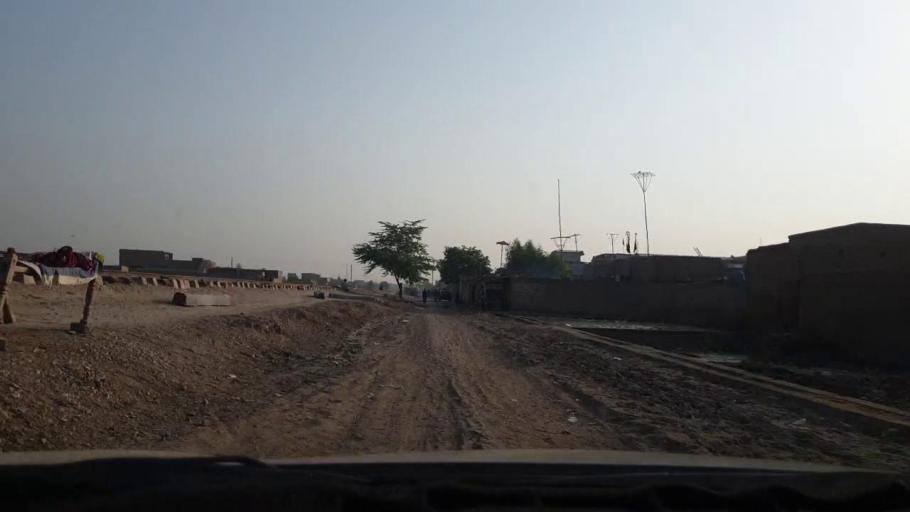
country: PK
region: Sindh
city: Larkana
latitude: 27.5321
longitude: 68.2012
